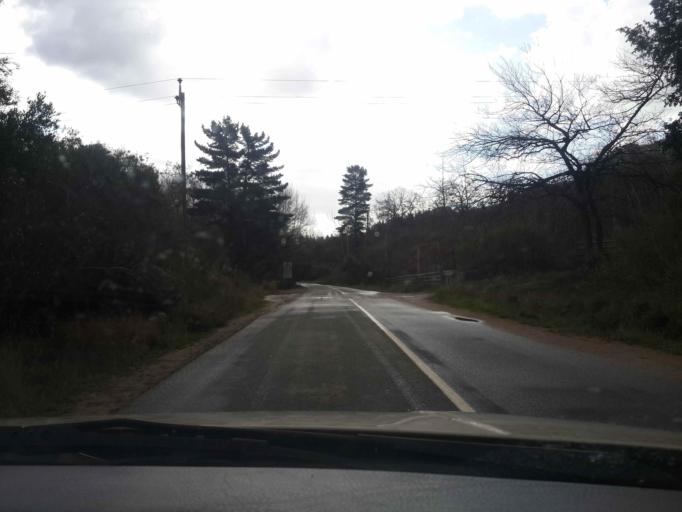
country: ZA
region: Western Cape
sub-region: Cape Winelands District Municipality
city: Stellenbosch
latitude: -33.9672
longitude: 18.9333
